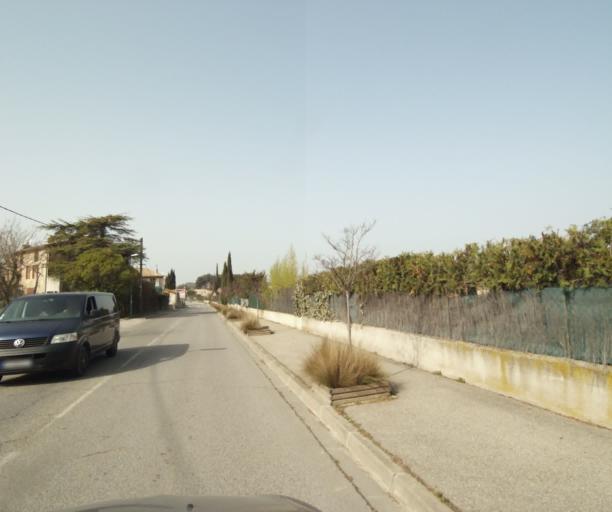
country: FR
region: Provence-Alpes-Cote d'Azur
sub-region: Departement des Bouches-du-Rhone
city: Simiane-Collongue
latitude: 43.4312
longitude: 5.4342
